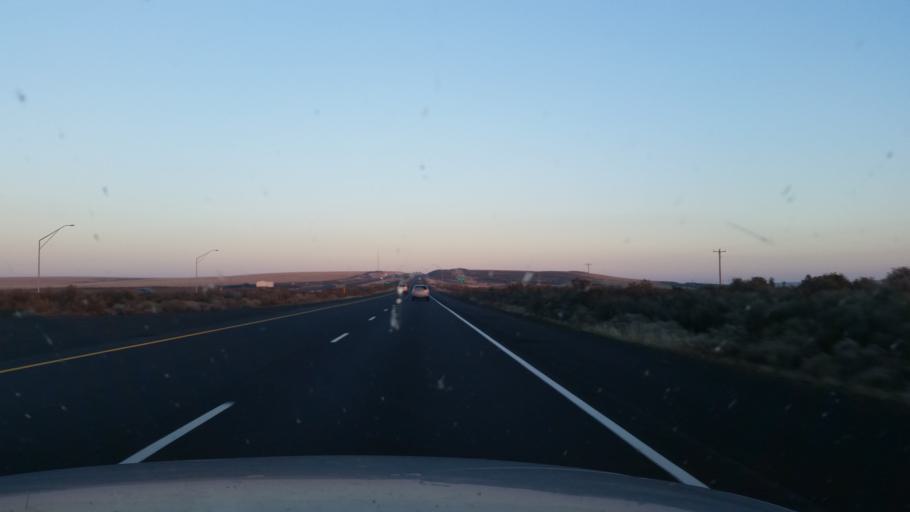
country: US
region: Washington
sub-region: Grant County
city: Warden
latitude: 47.0870
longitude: -118.8863
